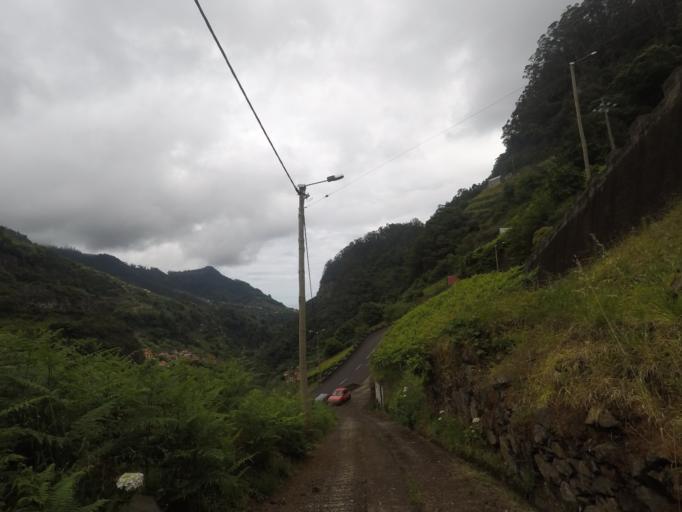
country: PT
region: Madeira
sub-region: Santana
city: Santana
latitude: 32.7614
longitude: -16.8771
